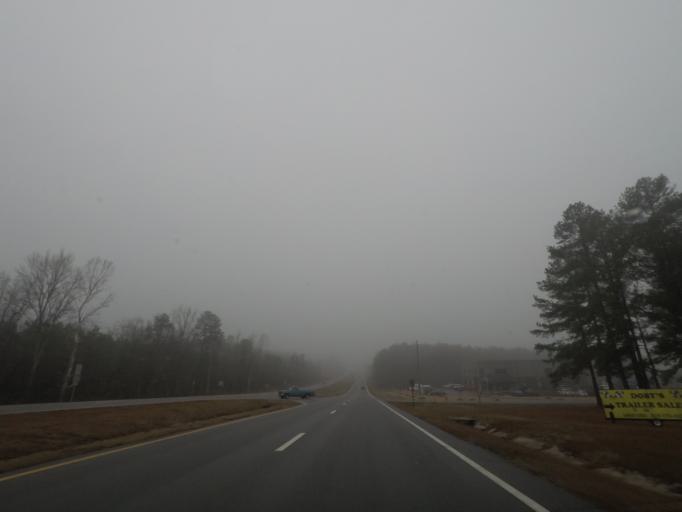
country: US
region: North Carolina
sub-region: Lee County
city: Sanford
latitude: 35.4023
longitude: -79.2316
